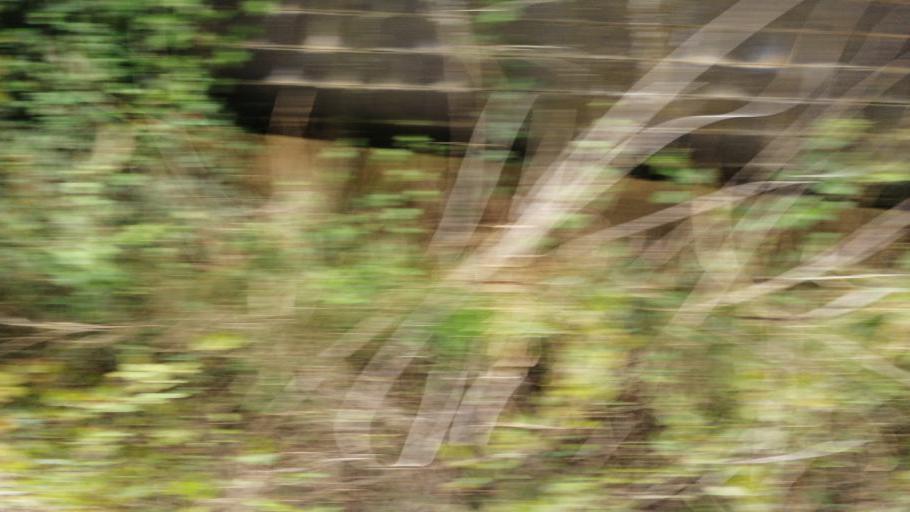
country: GB
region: Scotland
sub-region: Angus
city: Arbroath
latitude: 56.5575
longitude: -2.5910
